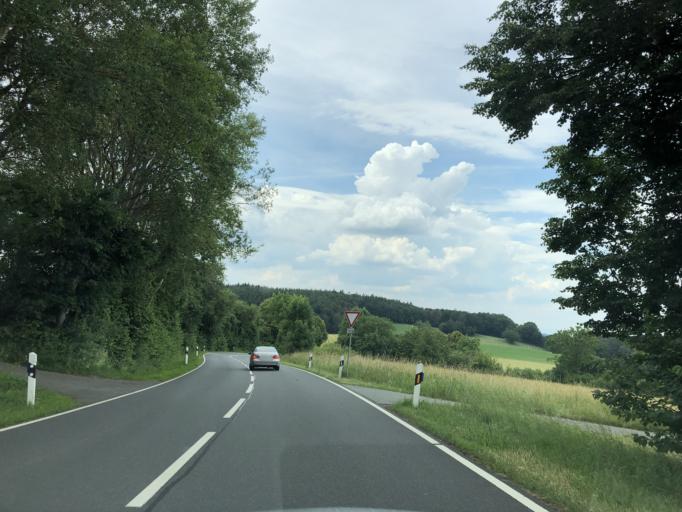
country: DE
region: Hesse
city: Lutzelbach
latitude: 49.7399
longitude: 8.7630
